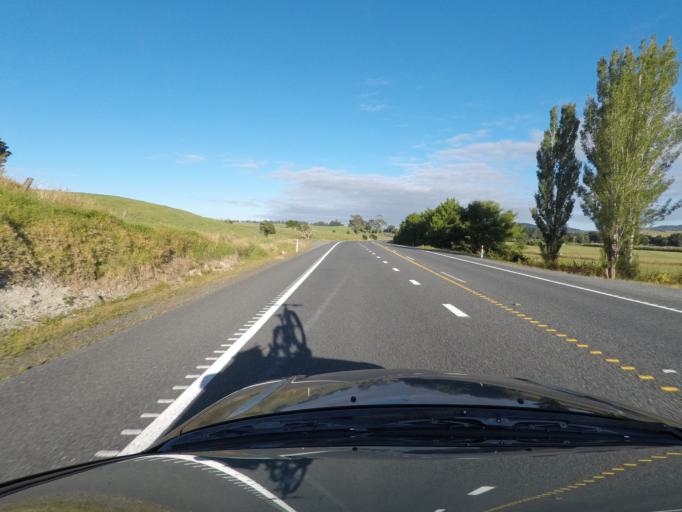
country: NZ
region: Northland
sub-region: Far North District
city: Kawakawa
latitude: -35.5171
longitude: 174.1912
